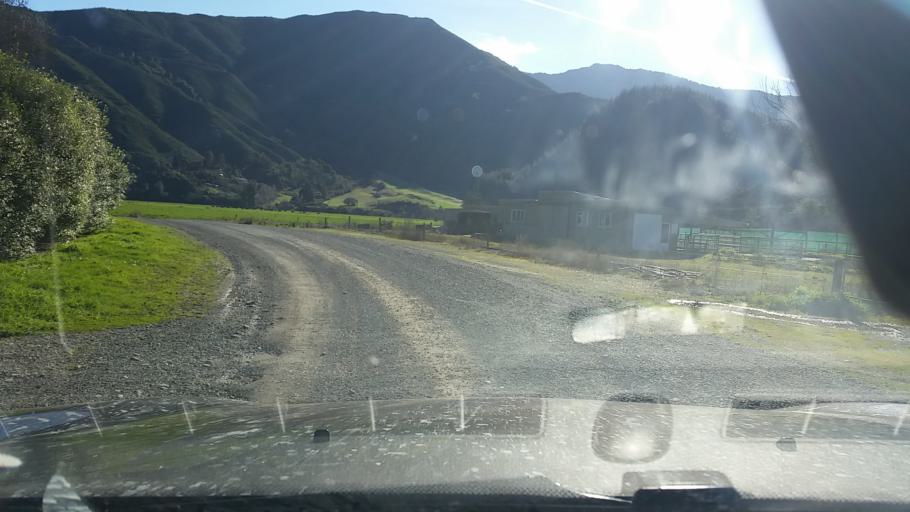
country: NZ
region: Marlborough
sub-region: Marlborough District
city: Picton
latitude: -41.2741
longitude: 173.7307
